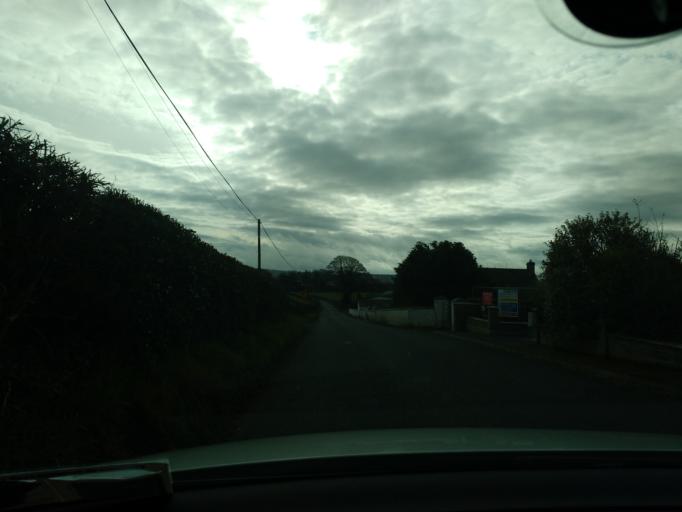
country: IE
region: Leinster
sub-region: Laois
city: Rathdowney
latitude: 52.6818
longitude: -7.6106
